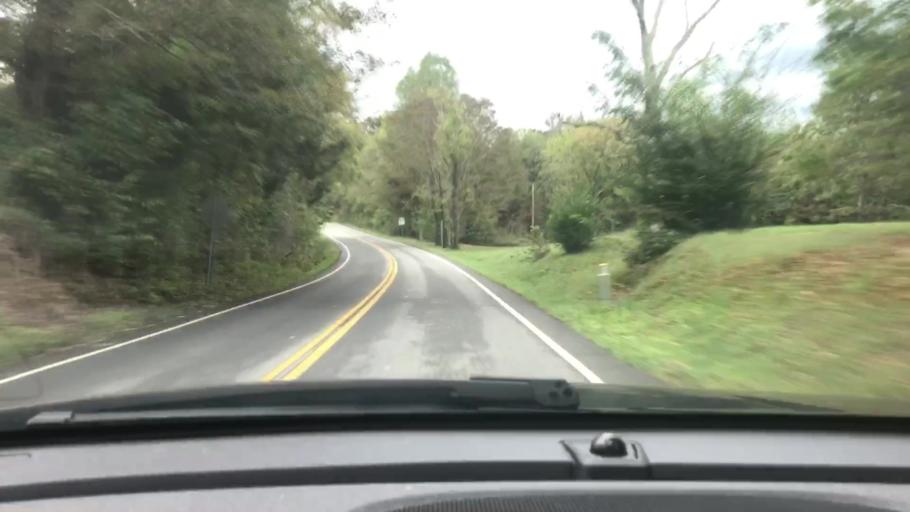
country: US
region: Tennessee
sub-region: Cheatham County
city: Ashland City
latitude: 36.2720
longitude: -87.1952
